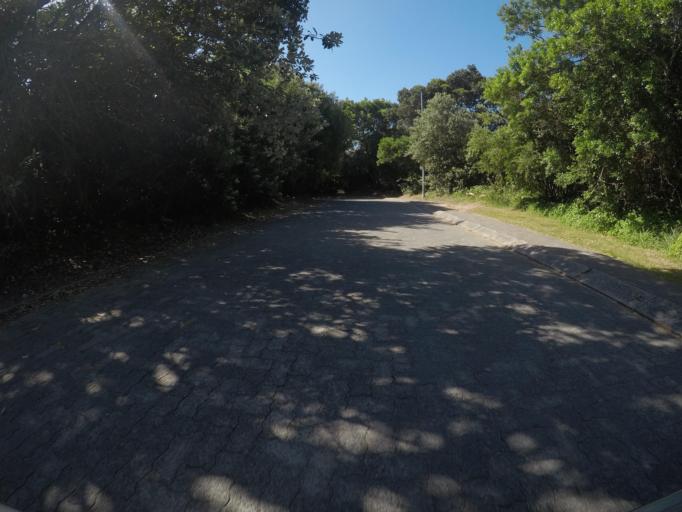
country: ZA
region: Eastern Cape
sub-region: Buffalo City Metropolitan Municipality
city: East London
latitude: -32.9860
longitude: 27.9486
